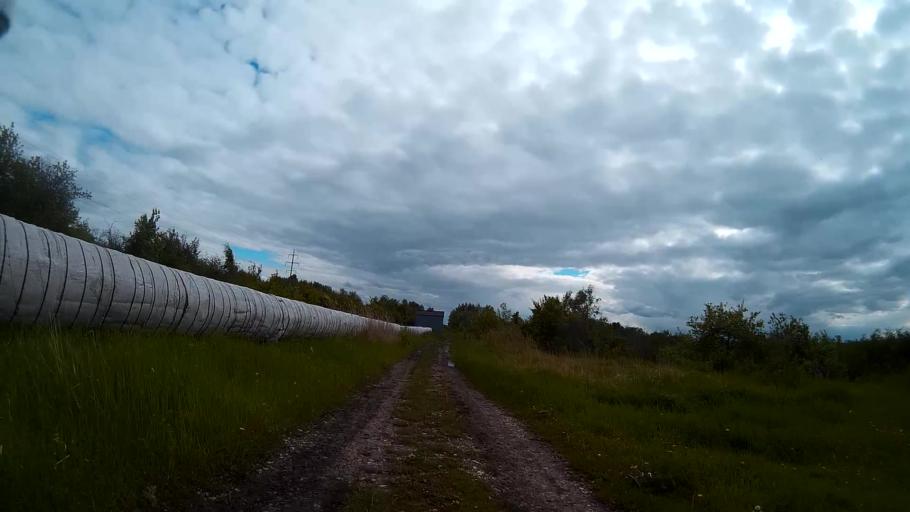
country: RU
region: Ulyanovsk
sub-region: Ulyanovskiy Rayon
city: Ulyanovsk
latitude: 54.2482
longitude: 48.3022
